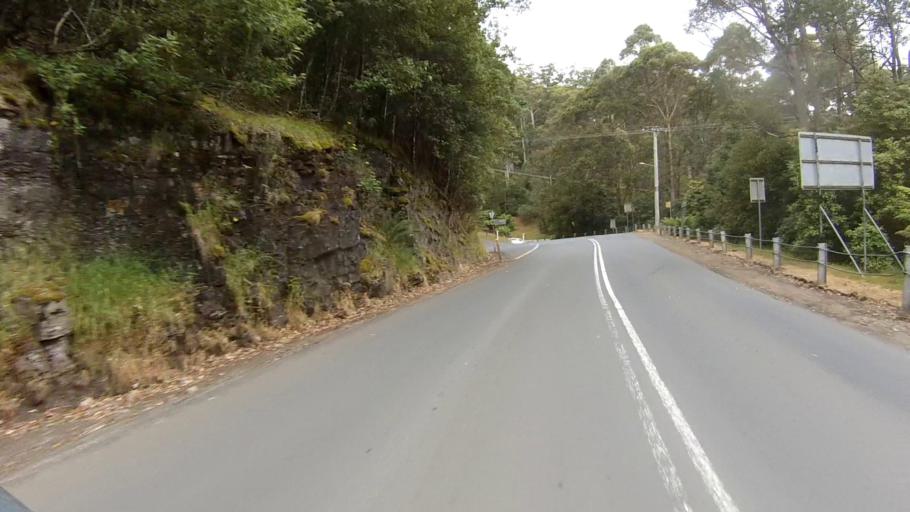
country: AU
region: Tasmania
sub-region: Hobart
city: Dynnyrne
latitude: -42.9207
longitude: 147.2597
